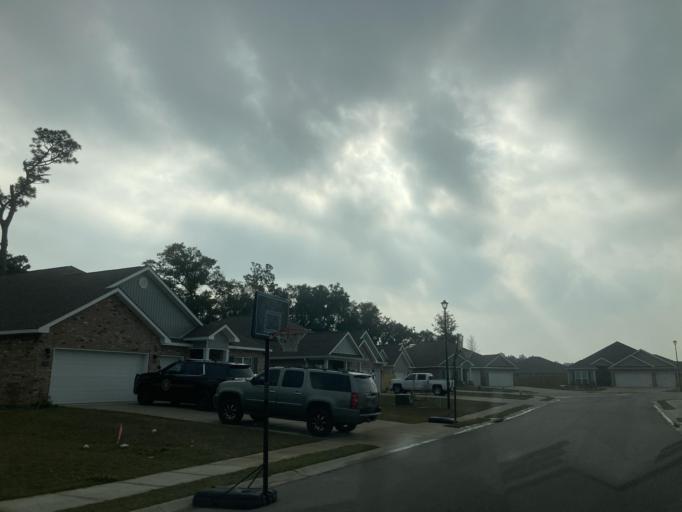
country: US
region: Mississippi
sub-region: Harrison County
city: Long Beach
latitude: 30.3759
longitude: -89.1583
